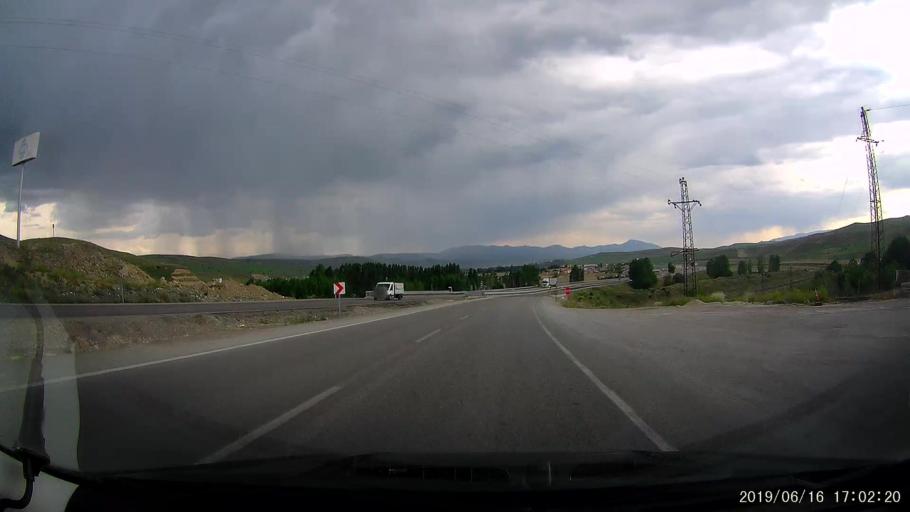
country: TR
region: Erzurum
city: Askale
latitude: 39.9407
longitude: 40.7565
